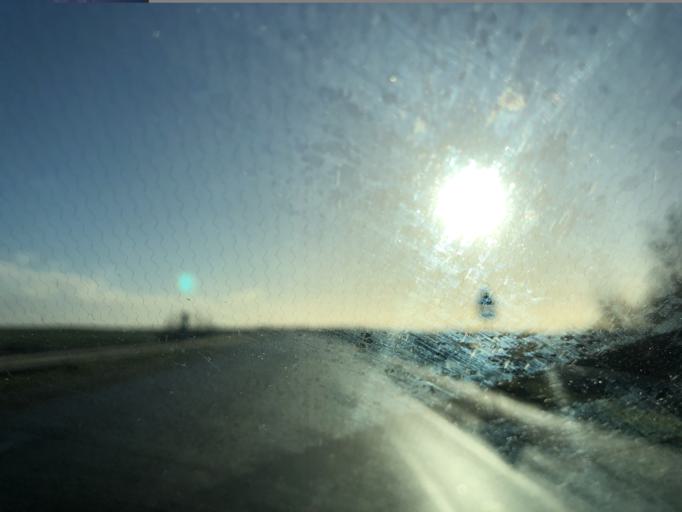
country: DK
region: Central Jutland
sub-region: Skive Kommune
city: Skive
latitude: 56.5477
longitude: 8.9934
